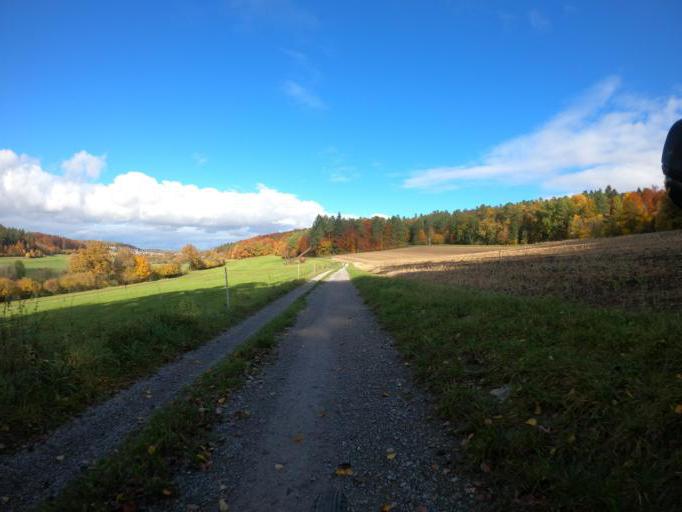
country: DE
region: Baden-Wuerttemberg
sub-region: Regierungsbezirk Stuttgart
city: Aidlingen
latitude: 48.7009
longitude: 8.9003
